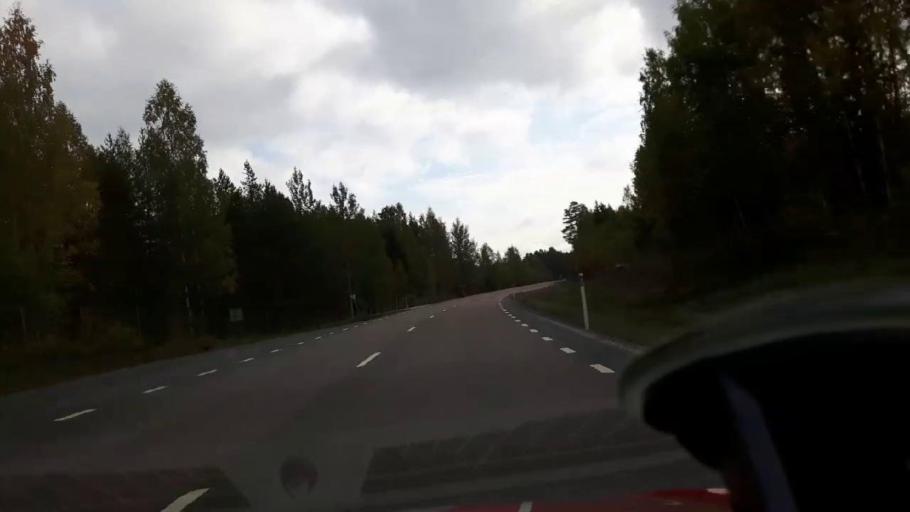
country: SE
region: Gaevleborg
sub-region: Bollnas Kommun
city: Kilafors
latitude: 61.2707
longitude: 16.5384
